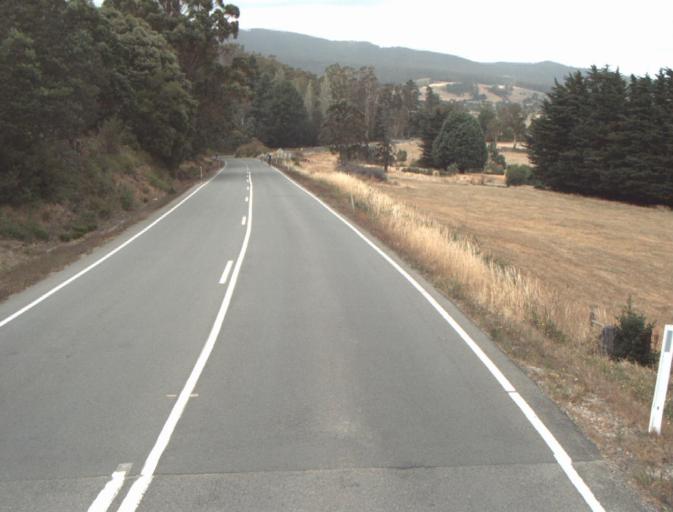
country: AU
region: Tasmania
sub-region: Launceston
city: Mayfield
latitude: -41.2256
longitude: 147.2066
